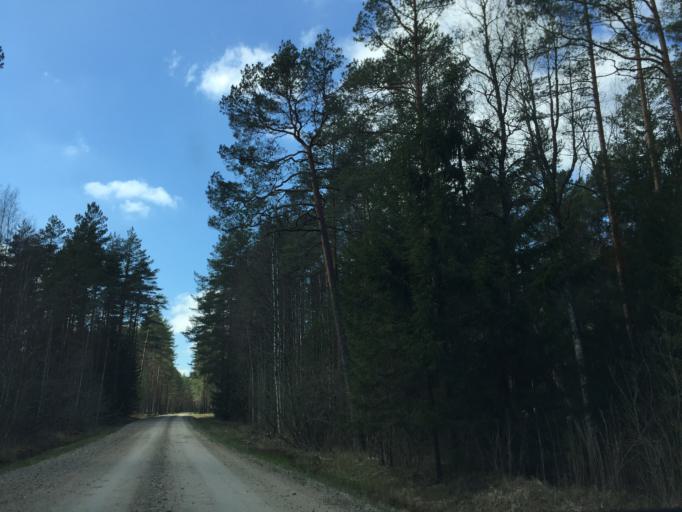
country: EE
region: Valgamaa
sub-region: Valga linn
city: Valga
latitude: 57.5930
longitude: 26.1133
